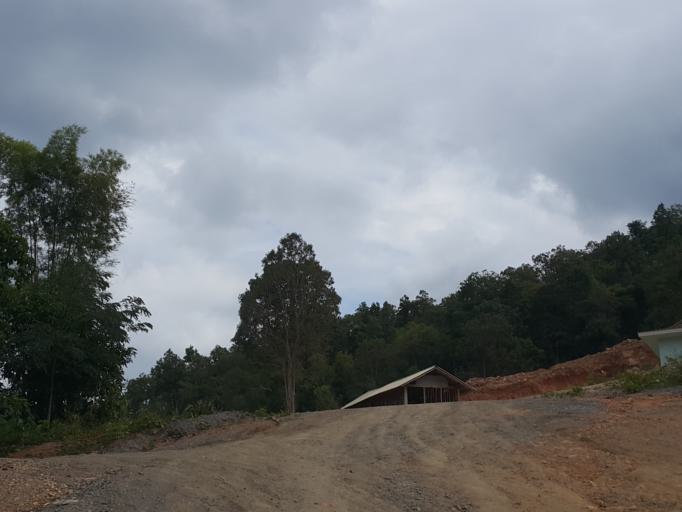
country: TH
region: Lampang
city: Chae Hom
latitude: 18.5717
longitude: 99.4392
